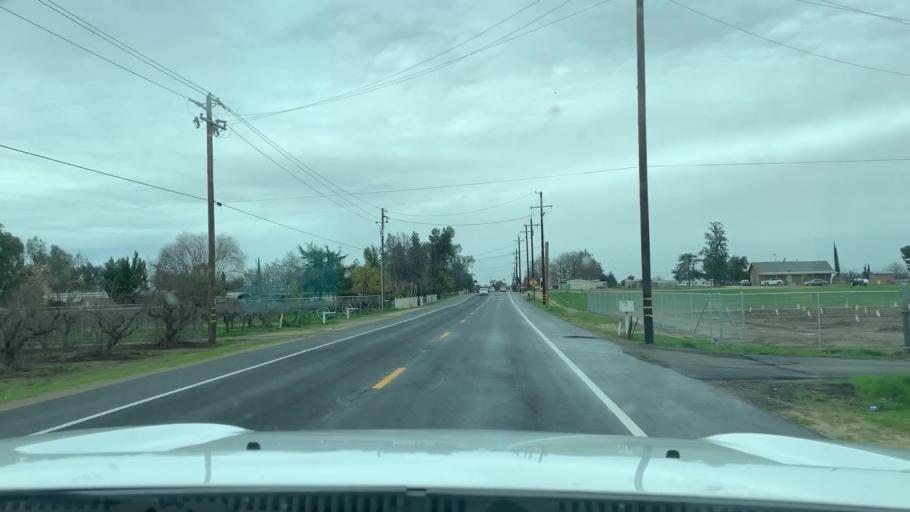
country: US
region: California
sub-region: Fresno County
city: Fowler
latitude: 36.5738
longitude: -119.6825
